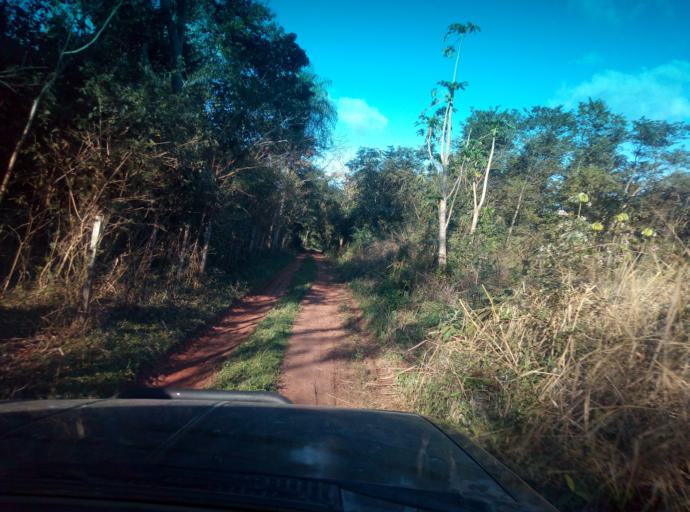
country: PY
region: Caaguazu
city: Carayao
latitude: -25.1824
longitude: -56.2632
